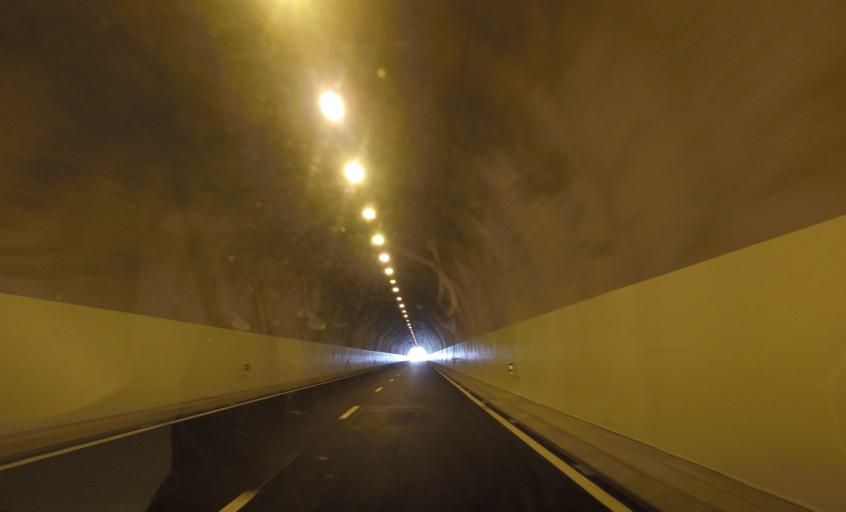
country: PT
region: Madeira
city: Camara de Lobos
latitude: 32.6648
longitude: -16.9693
